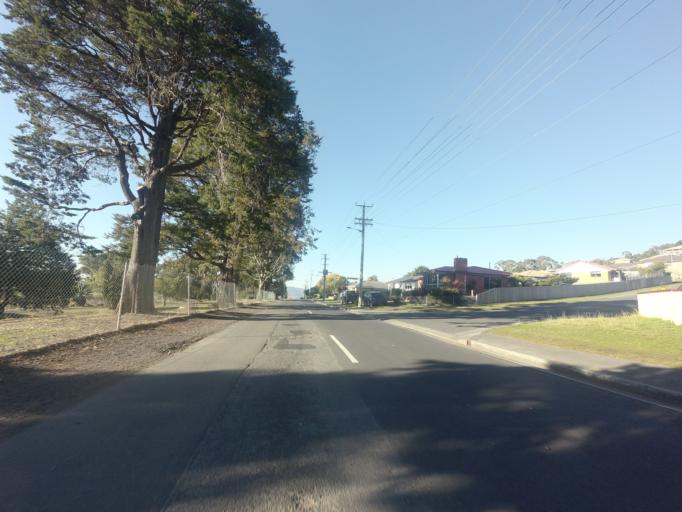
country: AU
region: Tasmania
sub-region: Glenorchy
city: West Moonah
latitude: -42.8518
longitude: 147.2549
